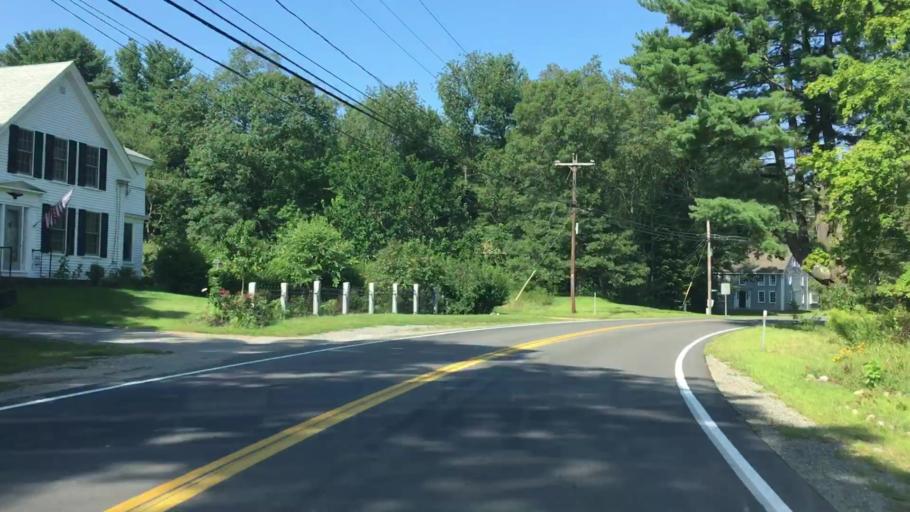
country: US
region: New Hampshire
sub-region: Rockingham County
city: East Kingston
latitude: 42.9251
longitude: -71.0161
